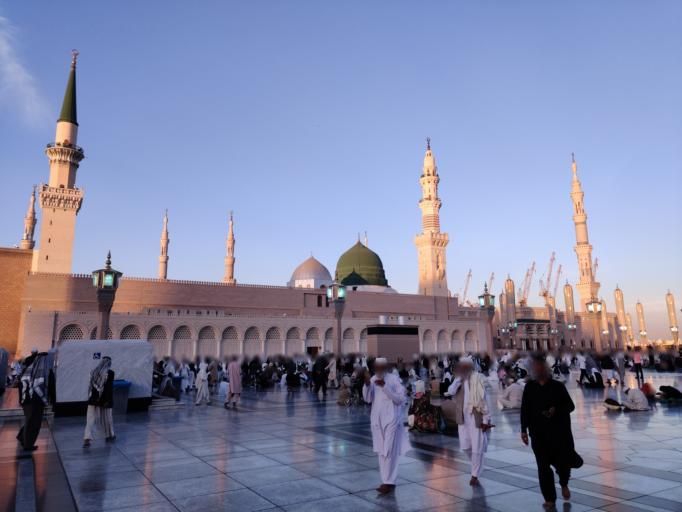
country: SA
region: Al Madinah al Munawwarah
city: Medina
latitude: 24.4666
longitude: 39.6107
